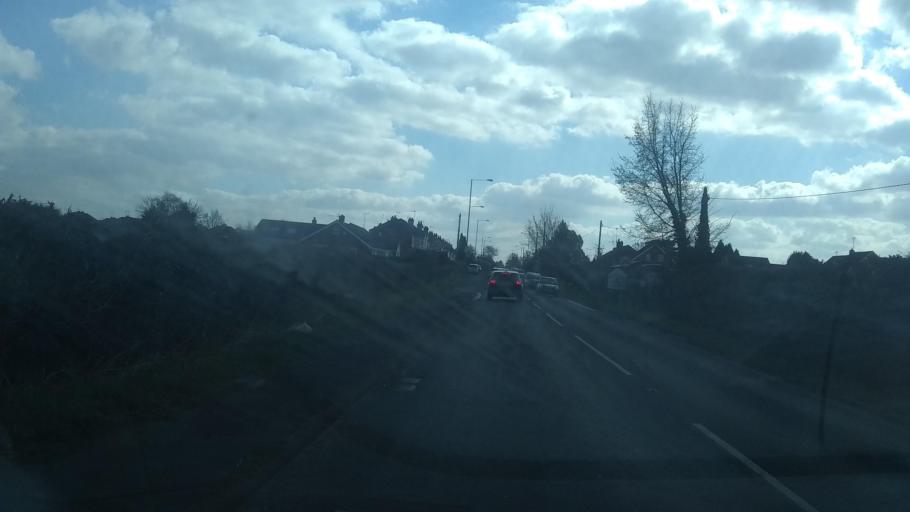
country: GB
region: England
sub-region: Worcestershire
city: Stourport-on-Severn
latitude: 52.3558
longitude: -2.2960
